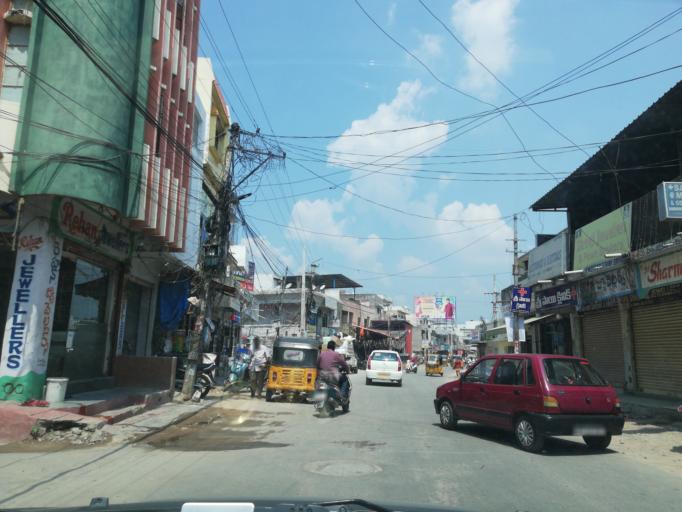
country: IN
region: Telangana
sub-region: Medak
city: Serilingampalle
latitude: 17.4909
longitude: 78.3171
